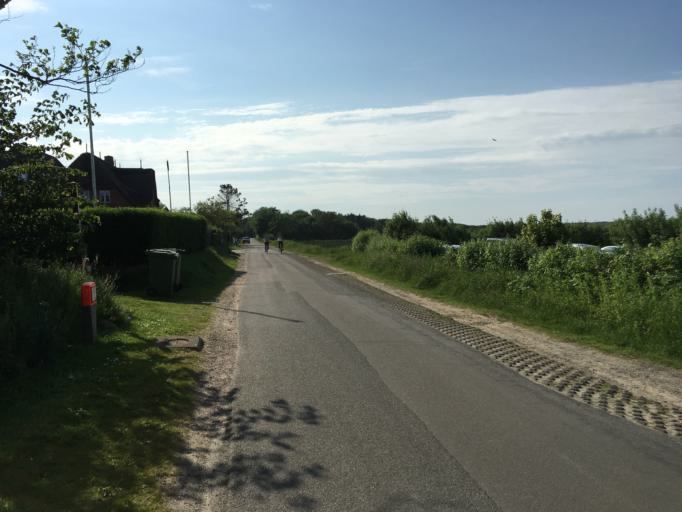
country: DE
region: Schleswig-Holstein
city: Norddorf
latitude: 54.6813
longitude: 8.3341
